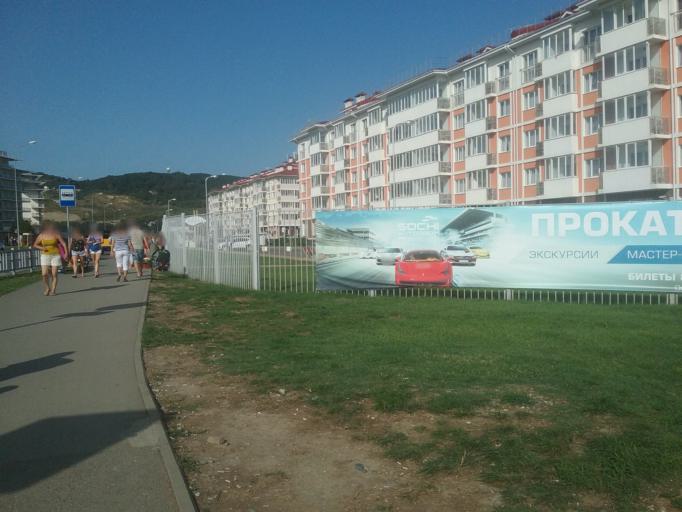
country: RU
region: Krasnodarskiy
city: Adler
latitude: 43.4007
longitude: 39.9773
